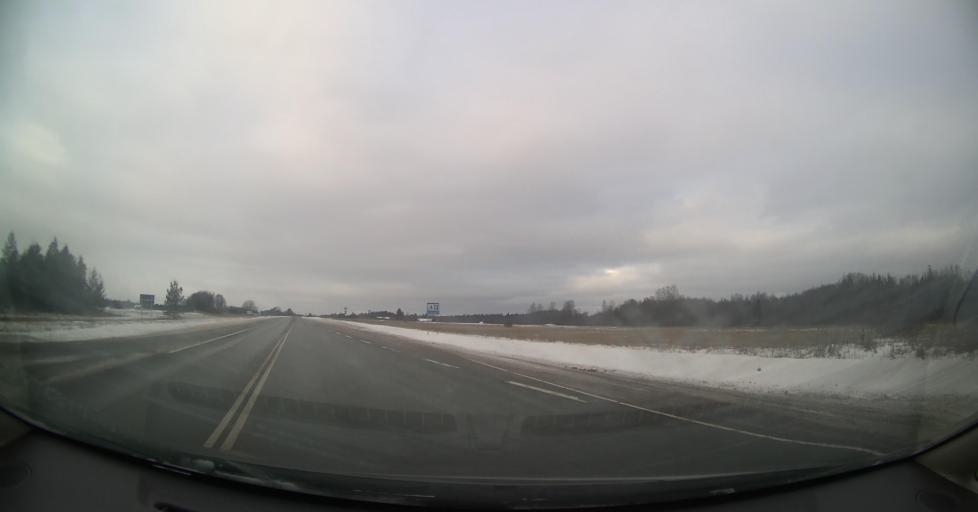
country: EE
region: Harju
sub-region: Anija vald
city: Kehra
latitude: 59.4017
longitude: 25.2742
